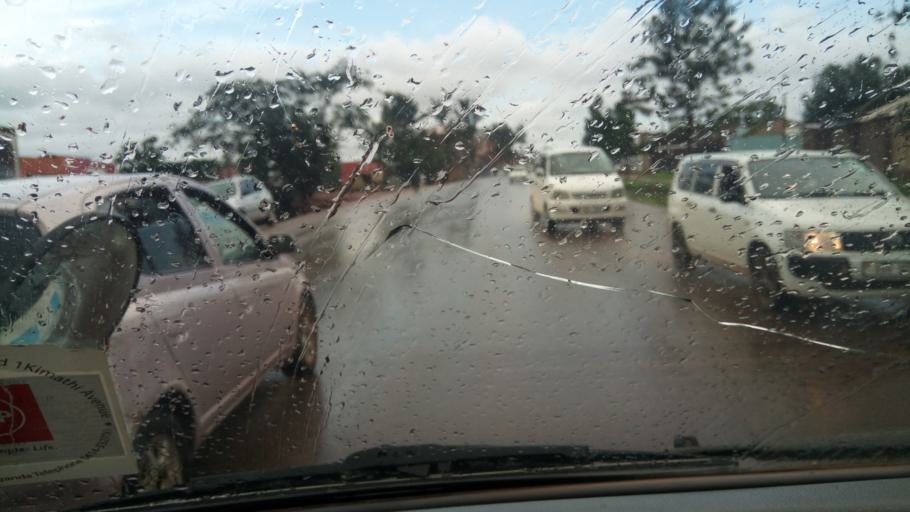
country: UG
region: Central Region
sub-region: Wakiso District
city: Wakiso
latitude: 0.3840
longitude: 32.5172
